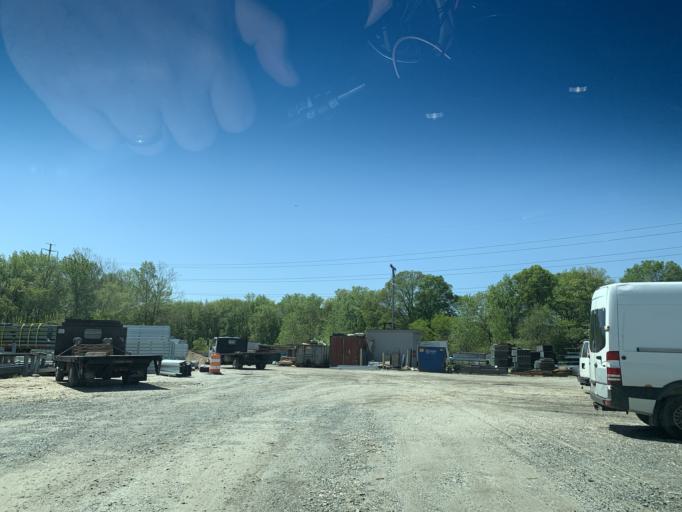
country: US
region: Maryland
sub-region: Baltimore County
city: Rossville
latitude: 39.3280
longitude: -76.4785
